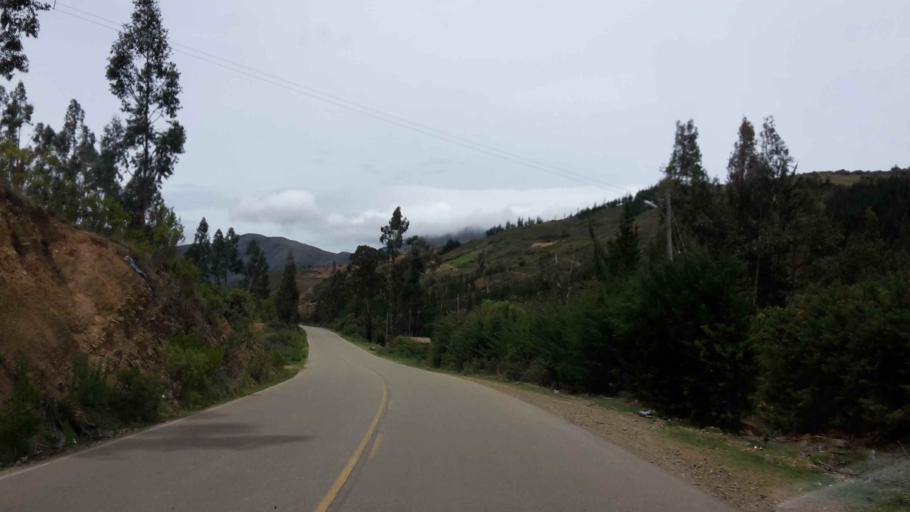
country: BO
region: Cochabamba
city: Totora
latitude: -17.6740
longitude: -65.2191
